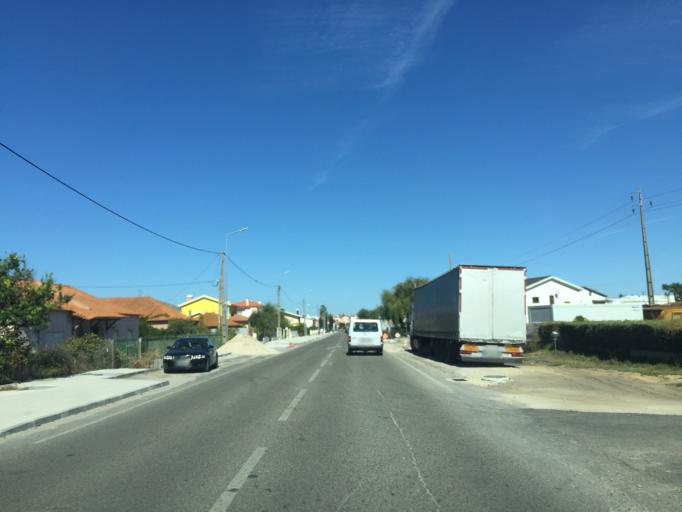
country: PT
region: Coimbra
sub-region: Montemor-O-Velho
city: Arazede
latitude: 40.3092
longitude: -8.7556
